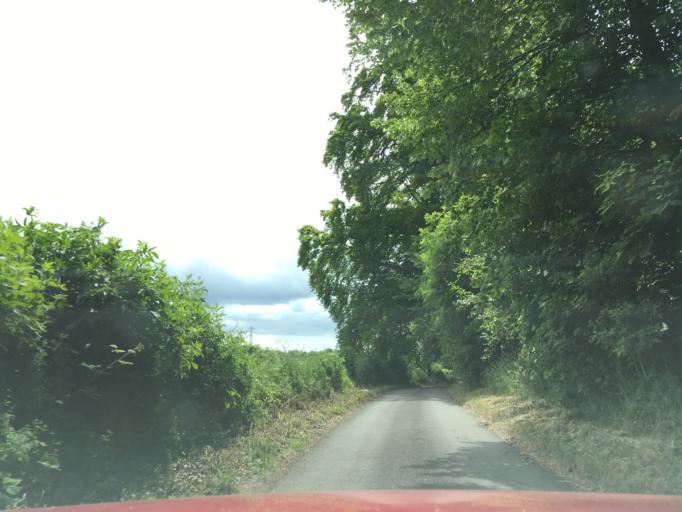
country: GB
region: England
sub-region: Gloucestershire
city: Cirencester
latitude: 51.7666
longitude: -1.9758
